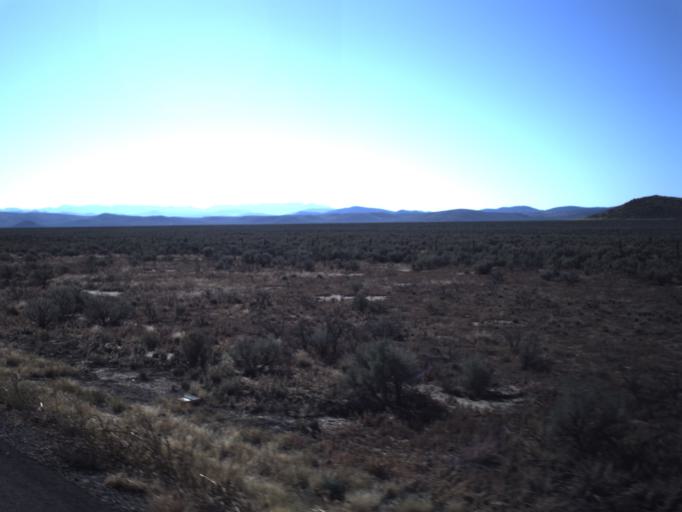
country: US
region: Utah
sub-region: Washington County
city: Enterprise
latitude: 37.7794
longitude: -113.8552
